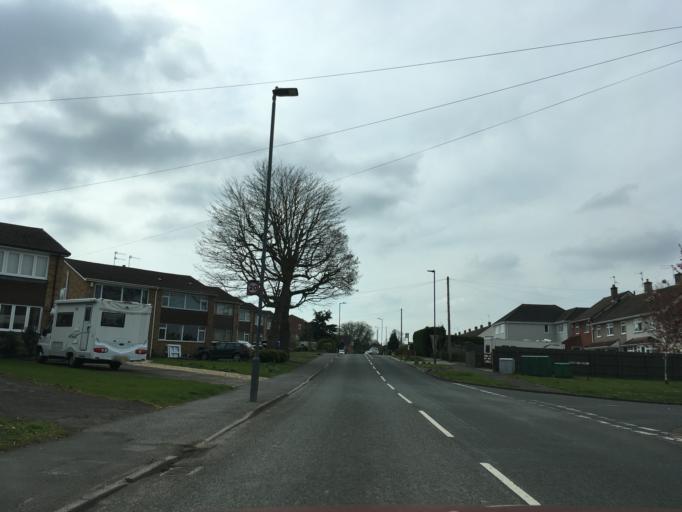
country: GB
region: England
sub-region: South Gloucestershire
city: Almondsbury
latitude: 51.5140
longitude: -2.5970
